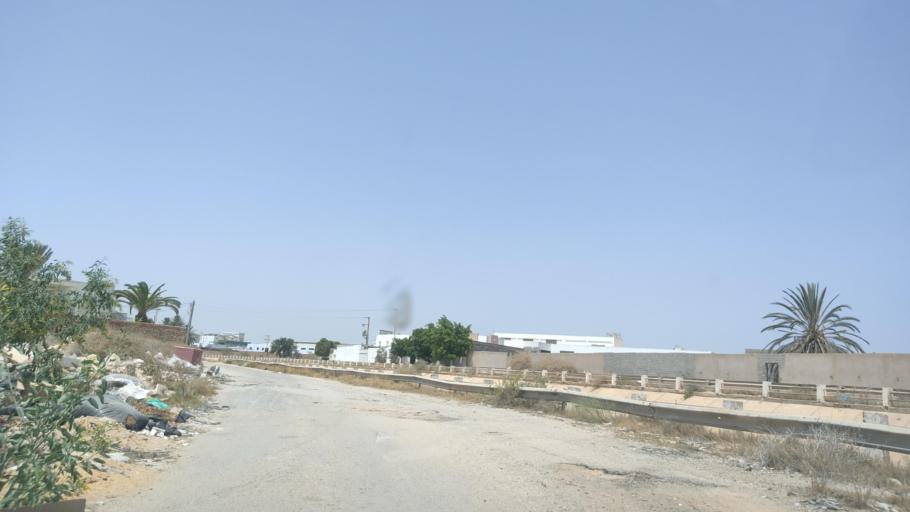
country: TN
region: Safaqis
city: Sfax
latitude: 34.7116
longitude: 10.7323
